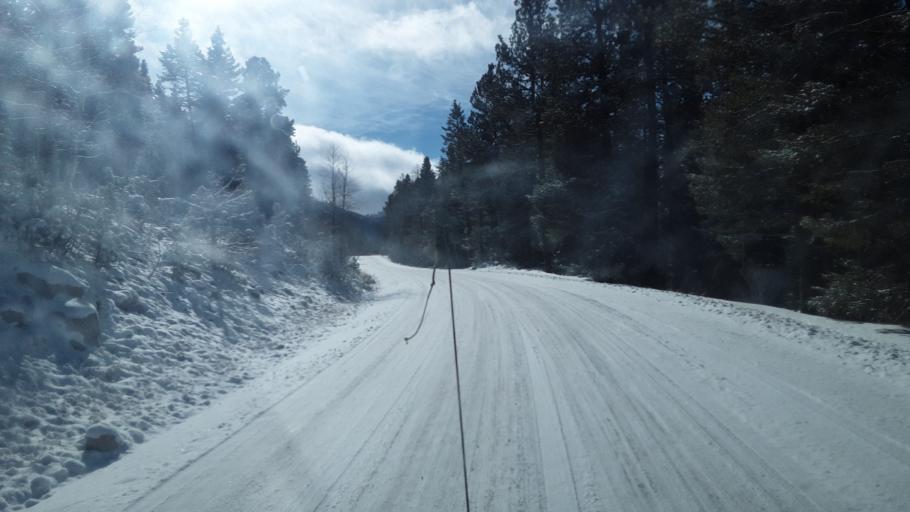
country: US
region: Colorado
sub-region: La Plata County
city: Bayfield
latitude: 37.4087
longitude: -107.6619
